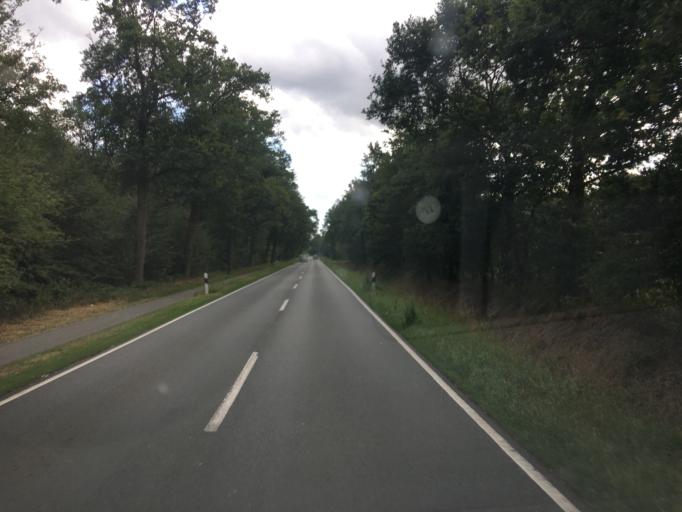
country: DE
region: Lower Saxony
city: Friesoythe
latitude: 53.0665
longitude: 7.8477
